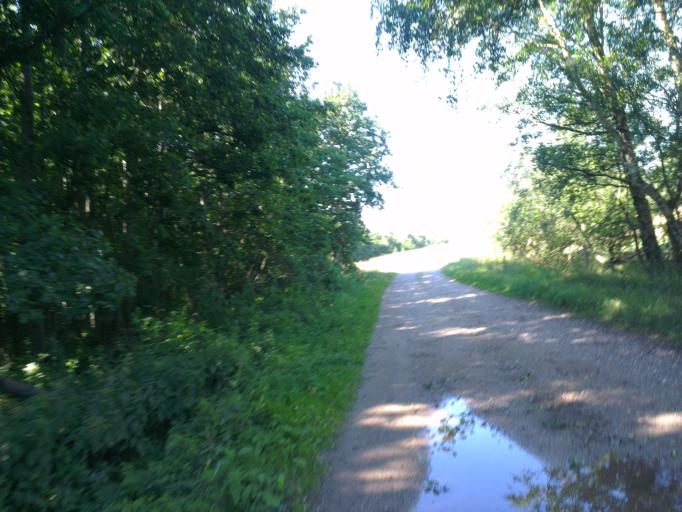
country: DK
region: Capital Region
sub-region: Frederikssund Kommune
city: Jaegerspris
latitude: 55.8915
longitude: 11.9512
